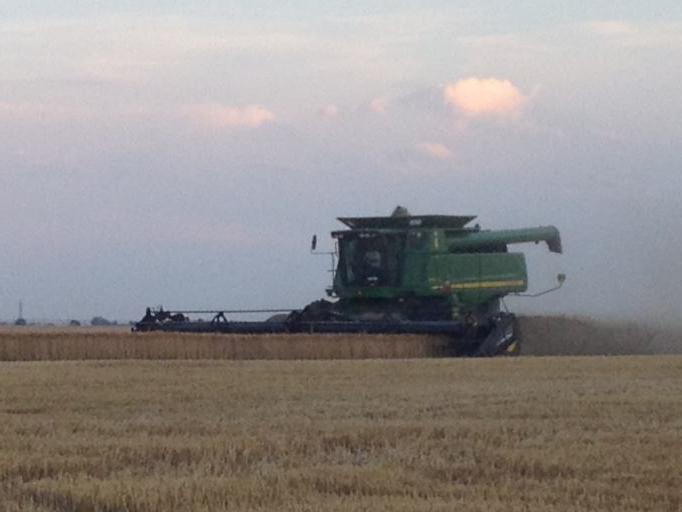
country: US
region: Oklahoma
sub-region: Alfalfa County
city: Helena
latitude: 36.6515
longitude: -98.0465
